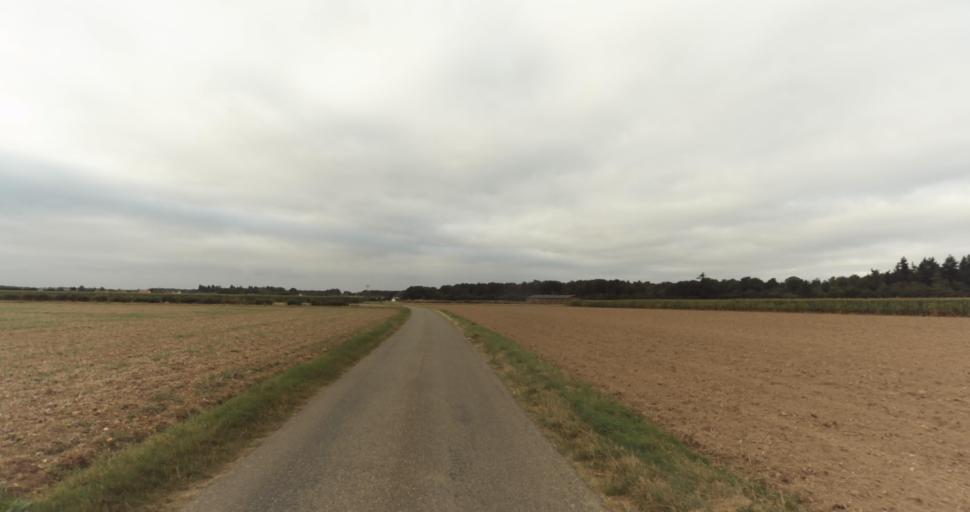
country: FR
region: Haute-Normandie
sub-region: Departement de l'Eure
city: Saint-Germain-sur-Avre
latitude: 48.7863
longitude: 1.2607
